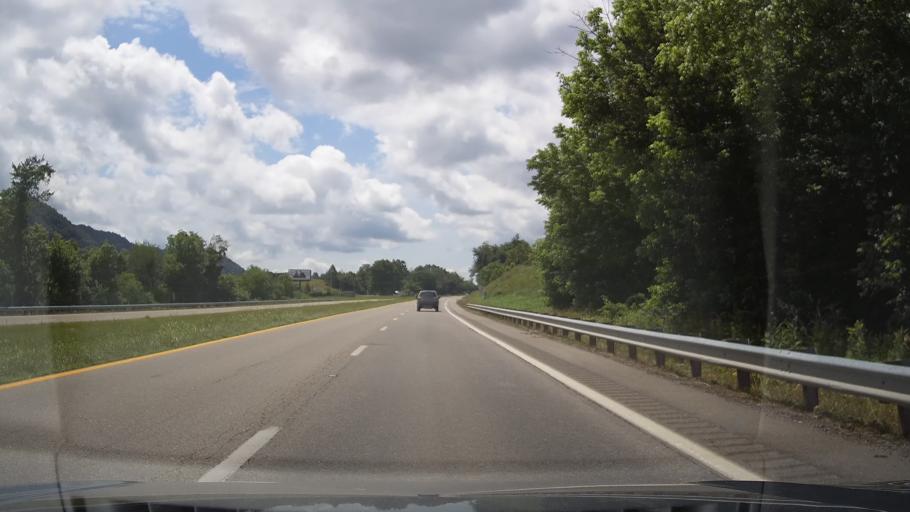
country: US
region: Tennessee
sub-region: Hawkins County
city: Mount Carmel
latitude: 36.6400
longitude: -82.6846
